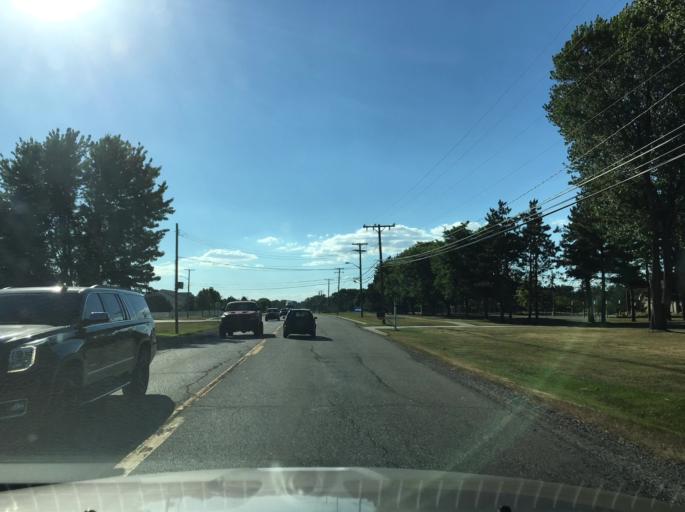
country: US
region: Michigan
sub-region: Macomb County
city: Sterling Heights
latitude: 42.5743
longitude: -82.9825
